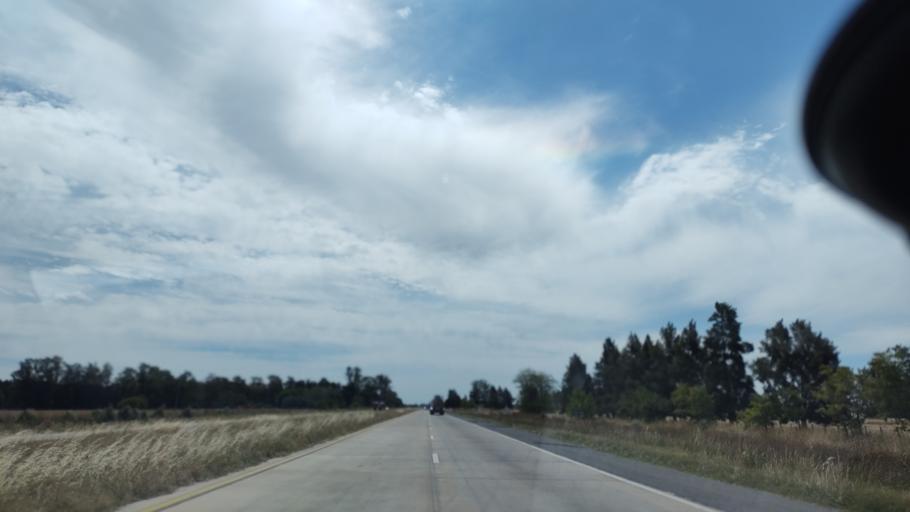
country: AR
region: Buenos Aires
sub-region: Partido de Brandsen
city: Brandsen
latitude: -35.0394
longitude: -58.1814
